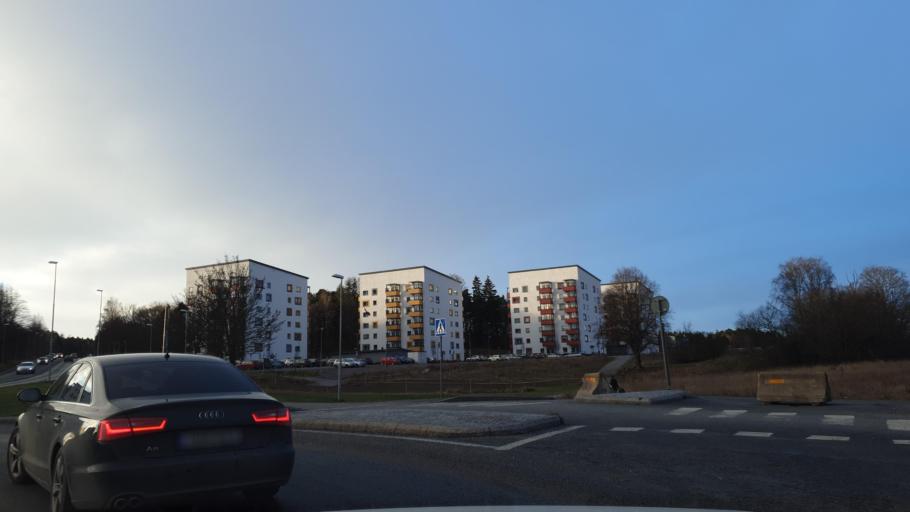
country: SE
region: Stockholm
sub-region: Sigtuna Kommun
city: Marsta
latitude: 59.6169
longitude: 17.8468
